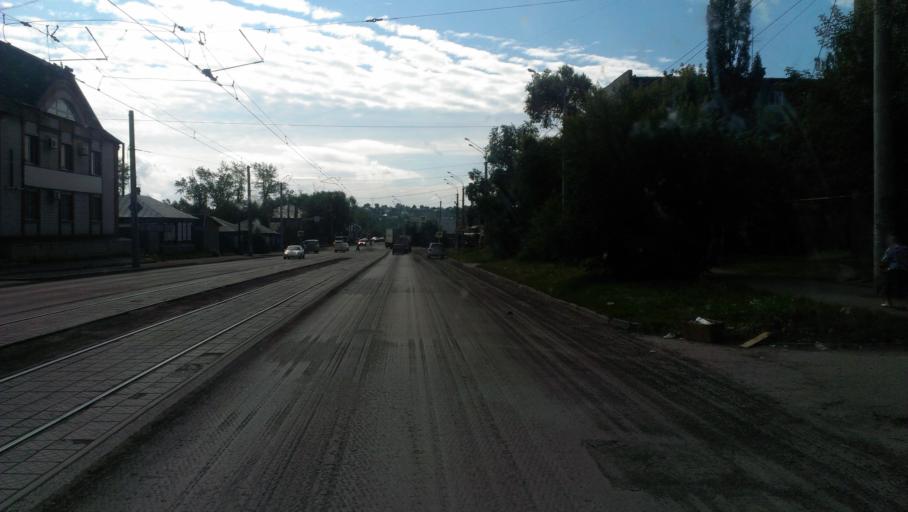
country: RU
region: Altai Krai
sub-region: Gorod Barnaulskiy
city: Barnaul
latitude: 53.3282
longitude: 83.7621
